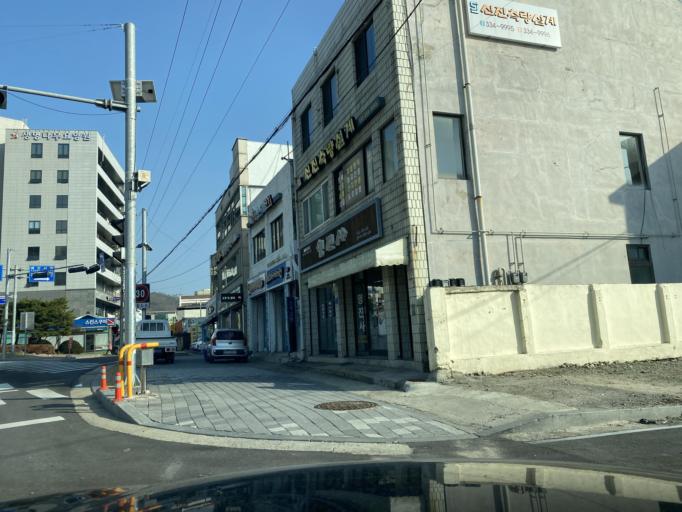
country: KR
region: Chungcheongnam-do
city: Yesan
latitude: 36.6785
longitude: 126.8444
